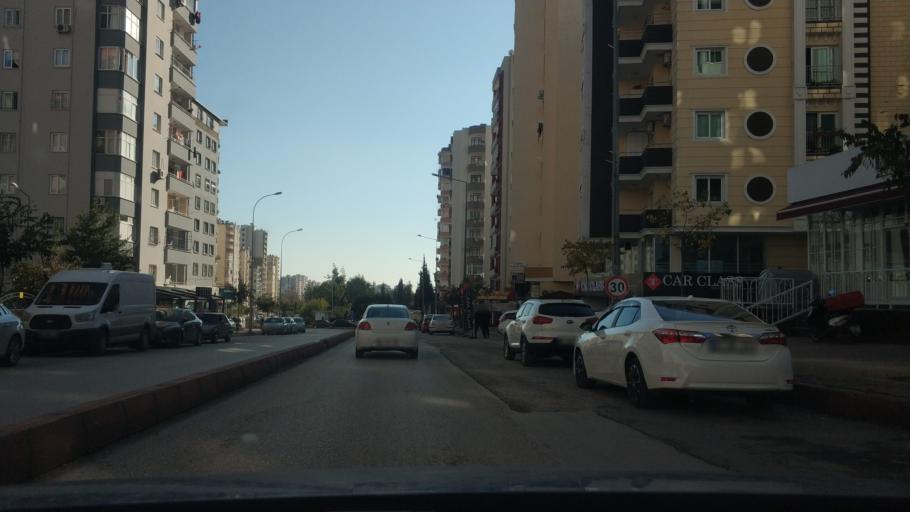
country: TR
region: Adana
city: Seyhan
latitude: 37.0534
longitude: 35.2768
